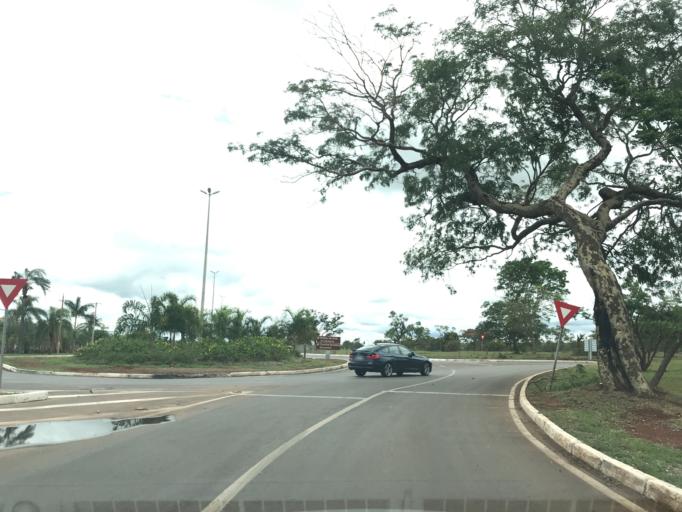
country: BR
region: Federal District
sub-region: Brasilia
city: Brasilia
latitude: -15.7902
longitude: -47.8344
